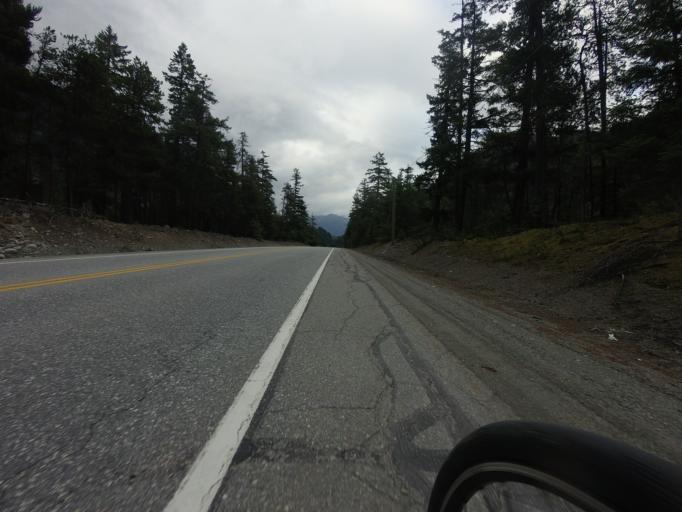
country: CA
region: British Columbia
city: Pemberton
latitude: 50.2768
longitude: -122.8636
